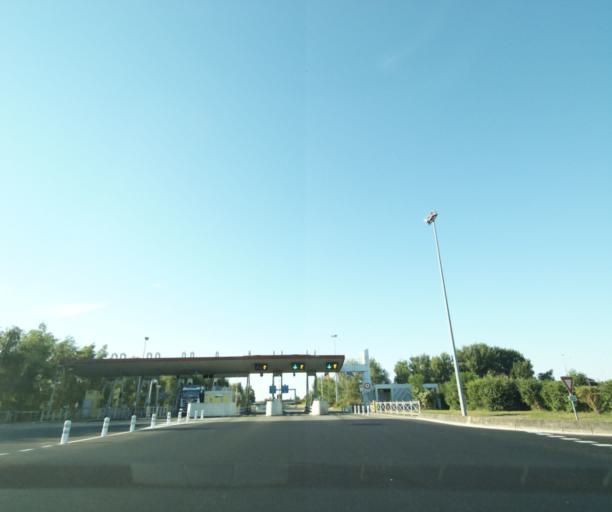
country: FR
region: Ile-de-France
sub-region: Departement de Seine-et-Marne
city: Marolles-sur-Seine
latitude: 48.3806
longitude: 3.0200
